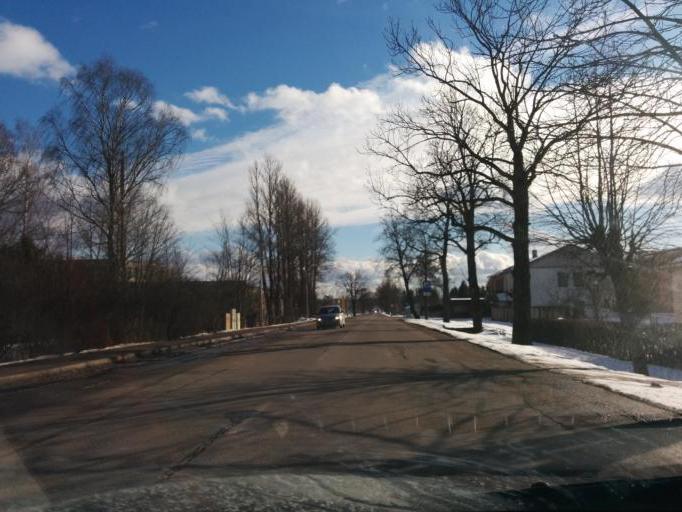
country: LV
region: Gulbenes Rajons
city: Gulbene
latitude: 57.1767
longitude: 26.7442
